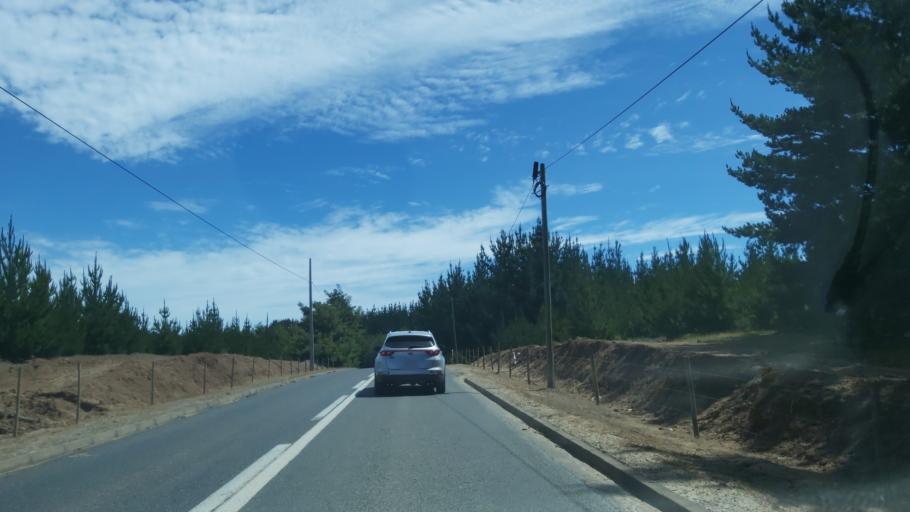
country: CL
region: Maule
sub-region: Provincia de Talca
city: Constitucion
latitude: -35.5202
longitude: -72.5338
